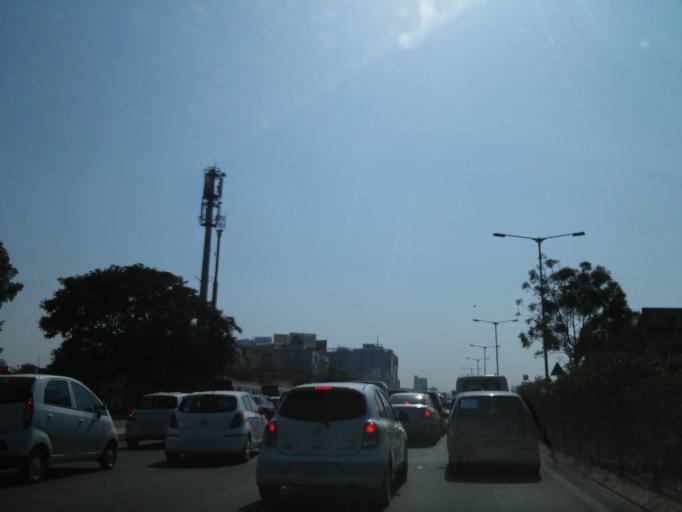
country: IN
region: Gujarat
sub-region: Ahmadabad
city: Ahmedabad
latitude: 23.0804
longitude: 72.5264
